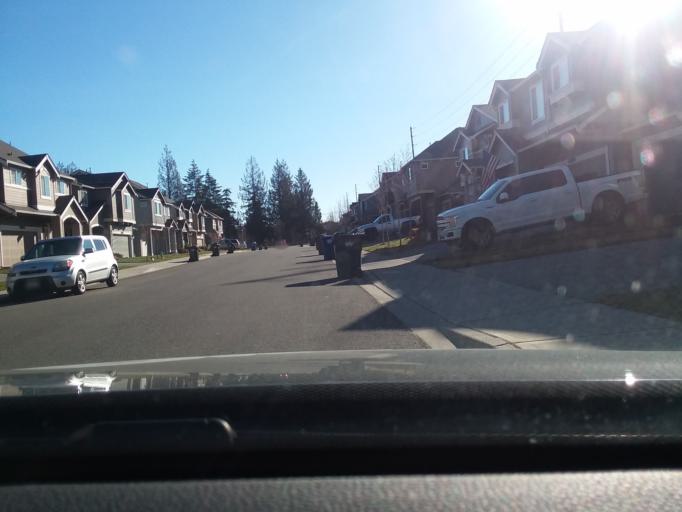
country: US
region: Washington
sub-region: Pierce County
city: Frederickson
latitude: 47.0969
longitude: -122.3222
